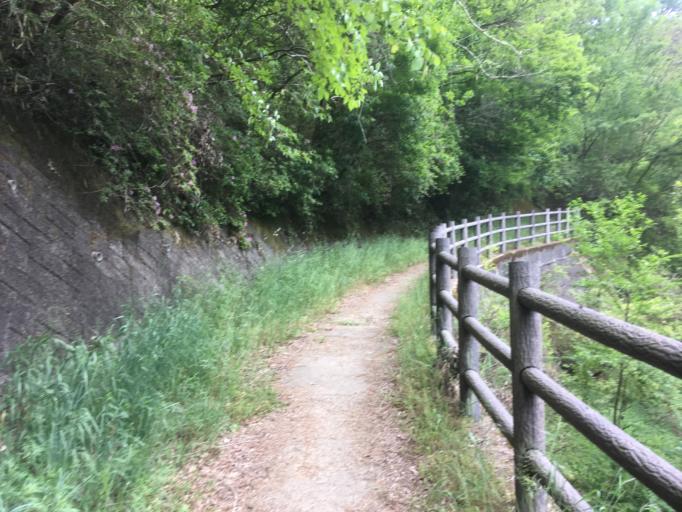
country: JP
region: Nara
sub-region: Ikoma-shi
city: Ikoma
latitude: 34.7050
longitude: 135.6715
